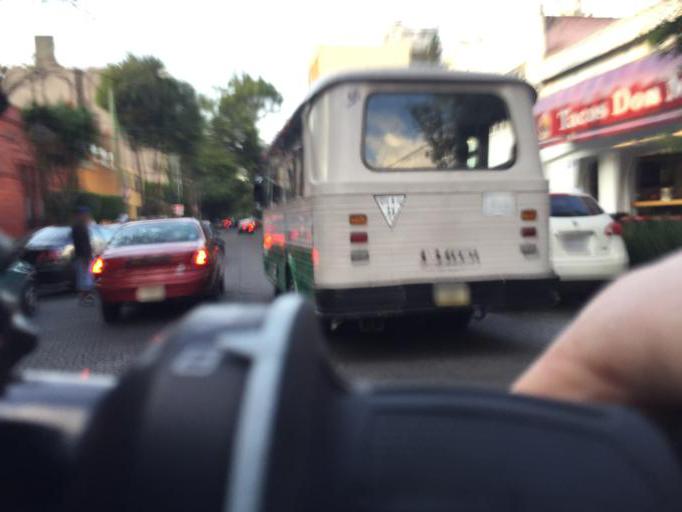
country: MX
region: Mexico City
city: Coyoacan
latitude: 19.3520
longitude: -99.1628
